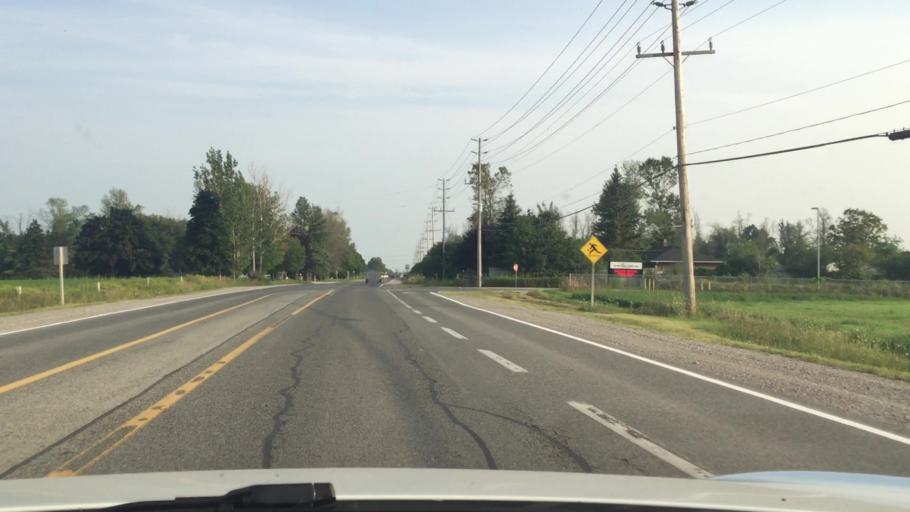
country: CA
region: Ontario
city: Oshawa
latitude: 43.9032
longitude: -78.7740
